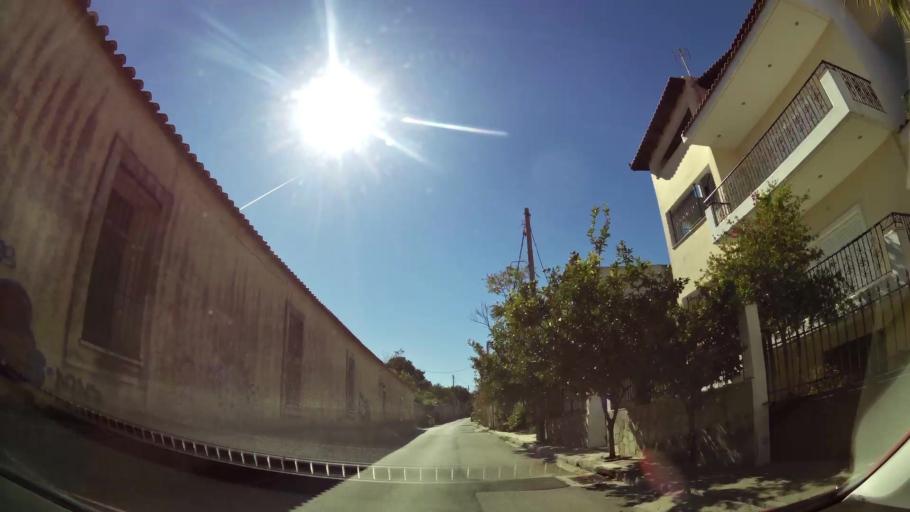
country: GR
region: Attica
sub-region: Nomarchia Anatolikis Attikis
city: Leondarion
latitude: 37.9888
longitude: 23.8634
